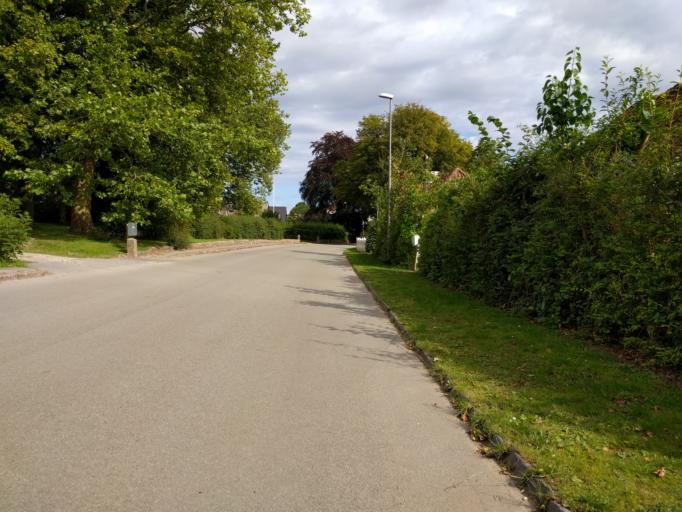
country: DK
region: South Denmark
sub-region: Kerteminde Kommune
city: Munkebo
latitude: 55.4672
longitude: 10.6033
